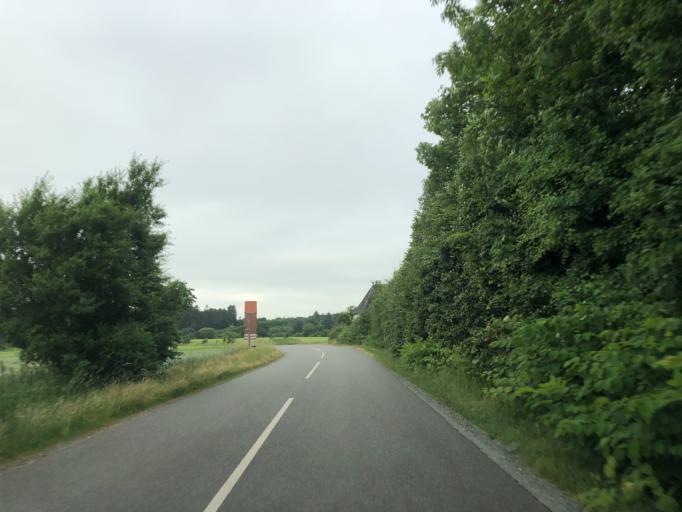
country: DK
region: Central Jutland
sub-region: Holstebro Kommune
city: Holstebro
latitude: 56.2483
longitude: 8.6258
